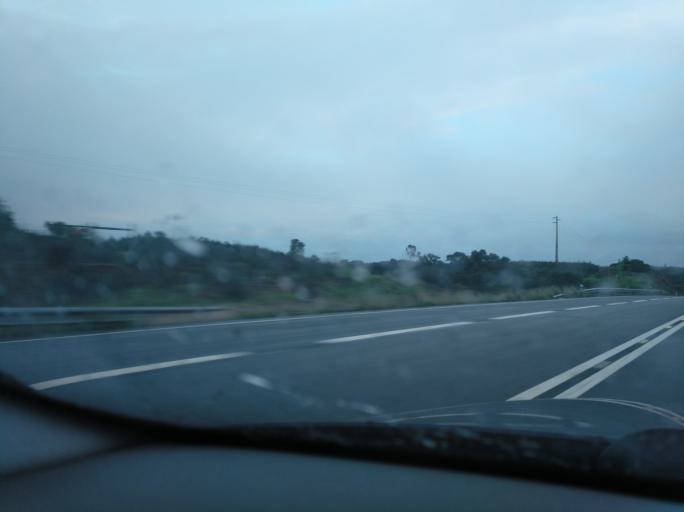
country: PT
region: Faro
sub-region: Castro Marim
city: Castro Marim
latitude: 37.3059
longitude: -7.4901
